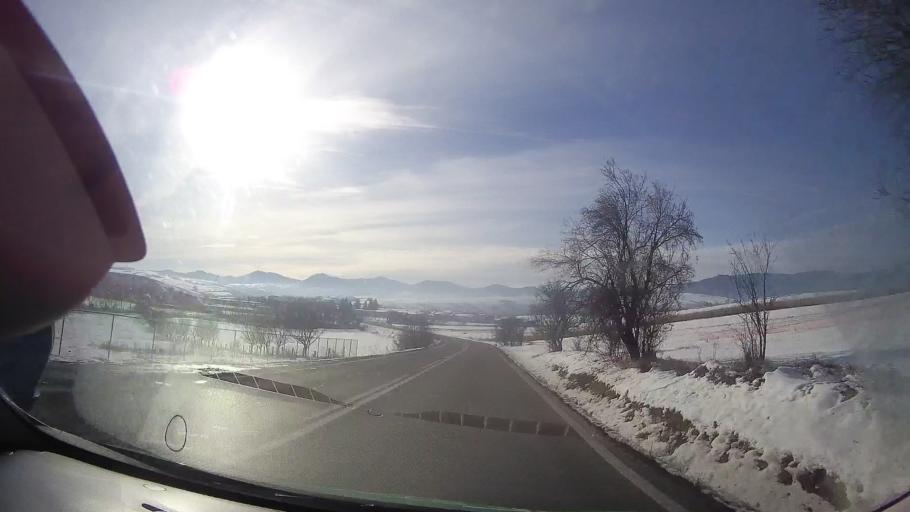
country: RO
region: Neamt
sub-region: Comuna Baltatesti
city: Valea Seaca
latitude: 47.1470
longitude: 26.3219
